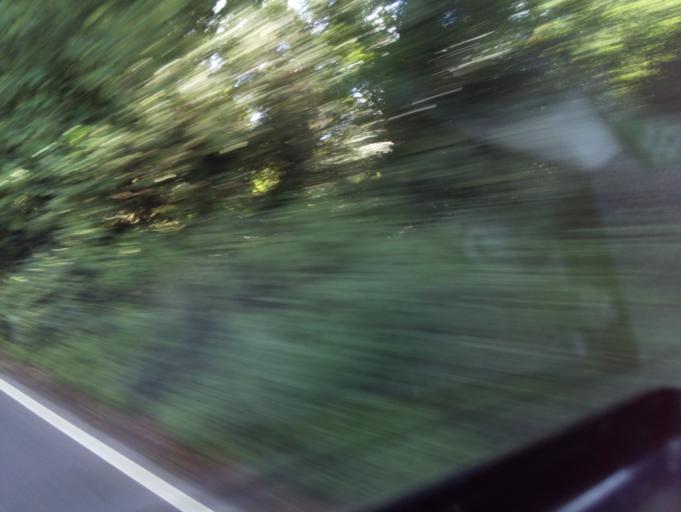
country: GB
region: England
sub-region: Herefordshire
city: Yatton
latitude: 51.9706
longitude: -2.5523
